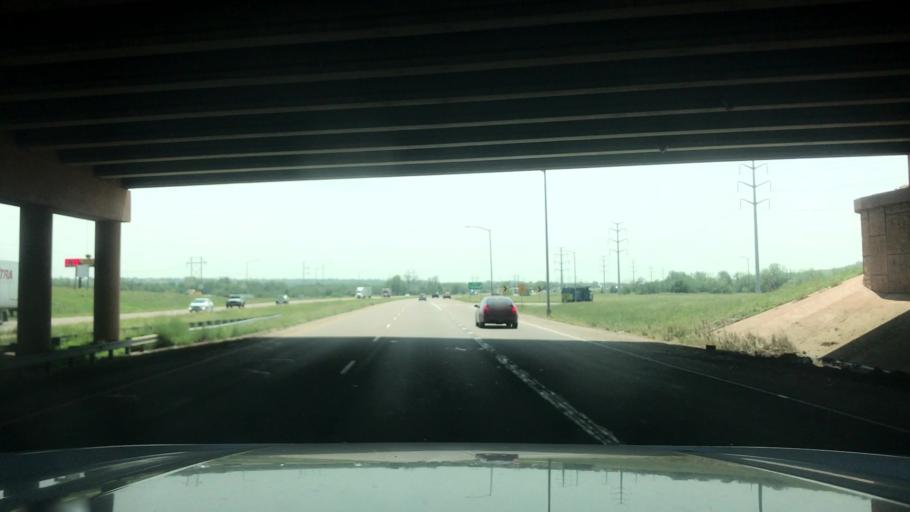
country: US
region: Colorado
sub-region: El Paso County
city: Security-Widefield
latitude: 38.7252
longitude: -104.7332
